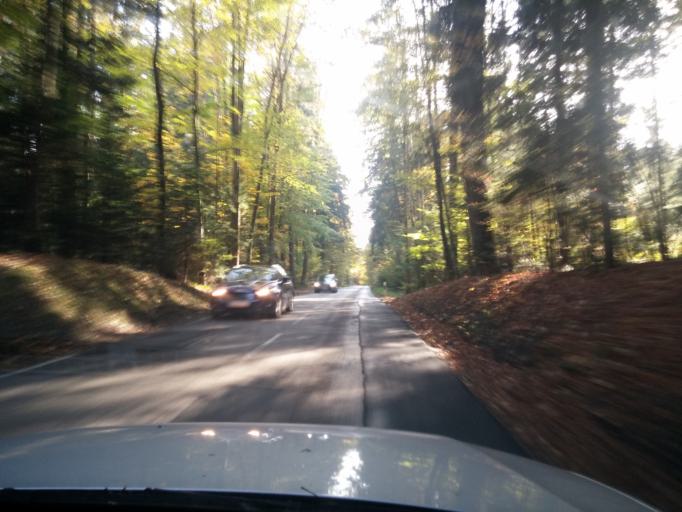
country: DE
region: Bavaria
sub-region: Upper Bavaria
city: Dietramszell
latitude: 47.8337
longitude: 11.5853
